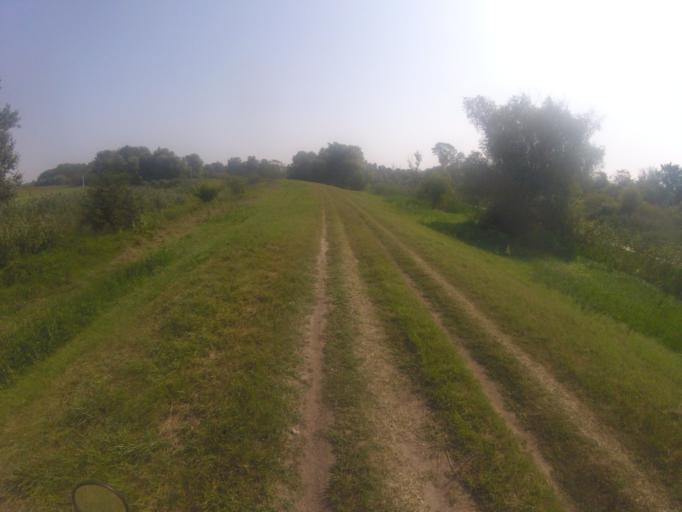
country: HU
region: Bacs-Kiskun
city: Baja
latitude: 46.1951
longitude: 18.9477
